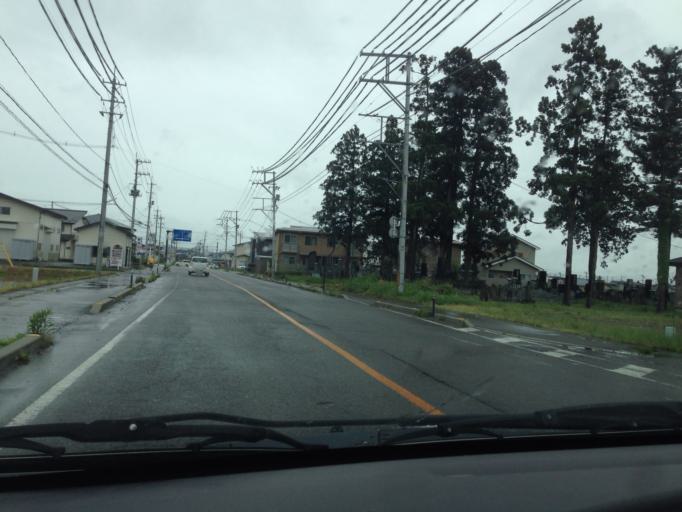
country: JP
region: Fukushima
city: Kitakata
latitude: 37.5547
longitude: 139.8301
